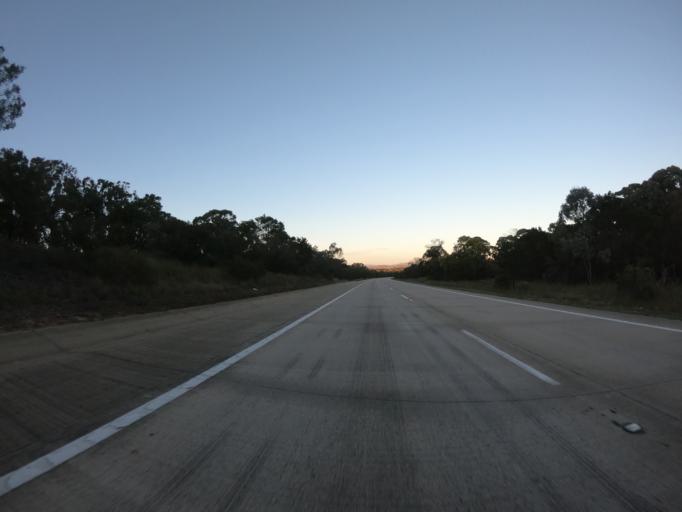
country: AU
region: New South Wales
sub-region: Goulburn Mulwaree
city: Goulburn
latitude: -34.7698
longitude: 149.7597
